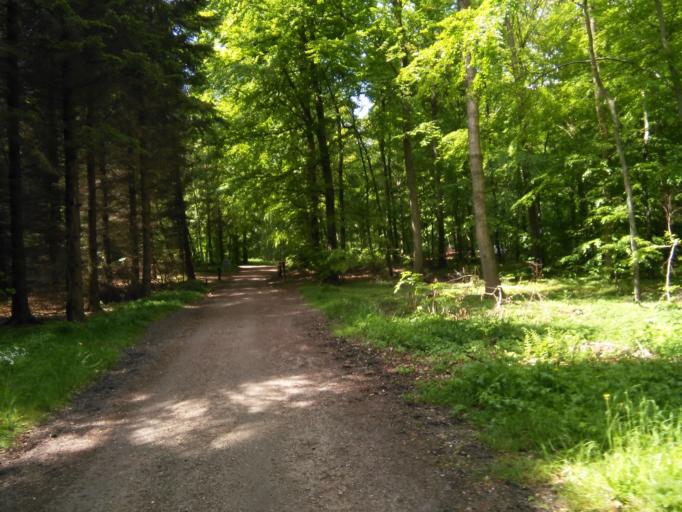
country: DK
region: Central Jutland
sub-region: Arhus Kommune
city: Beder
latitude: 56.0673
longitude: 10.2489
